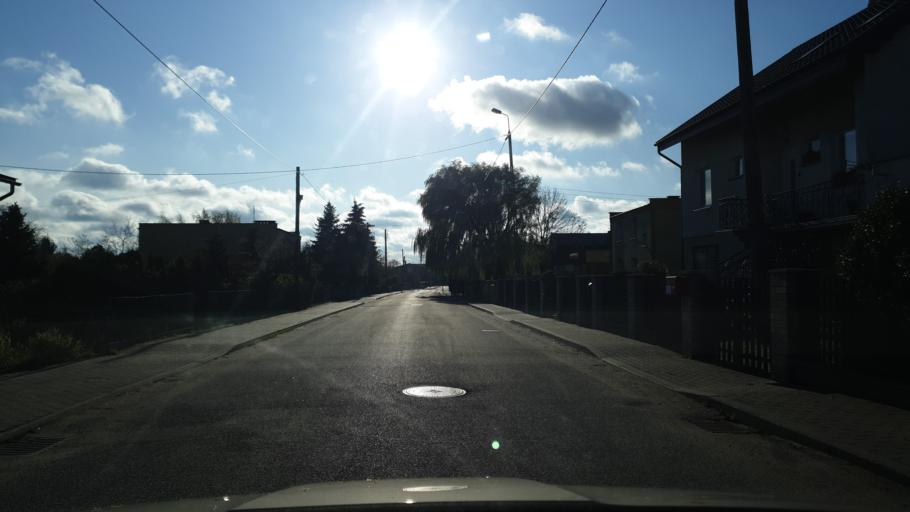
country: PL
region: Pomeranian Voivodeship
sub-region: Powiat pucki
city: Gniezdzewo
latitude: 54.7588
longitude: 18.3996
